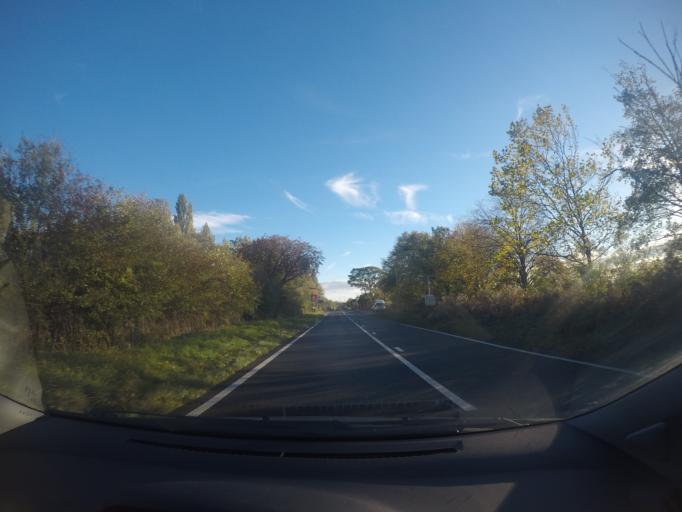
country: GB
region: England
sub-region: City of York
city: York
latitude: 53.9812
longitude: -1.0821
